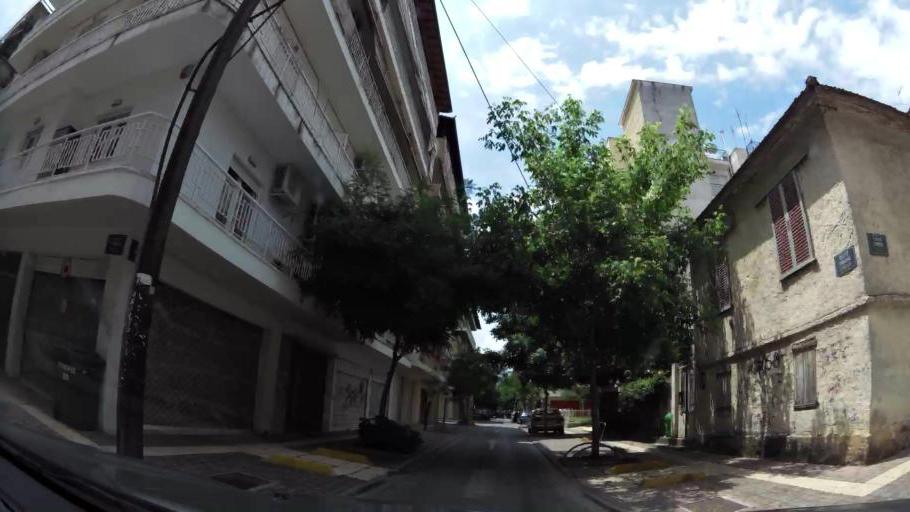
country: GR
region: Central Macedonia
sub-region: Nomos Pierias
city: Katerini
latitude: 40.2718
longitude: 22.5149
